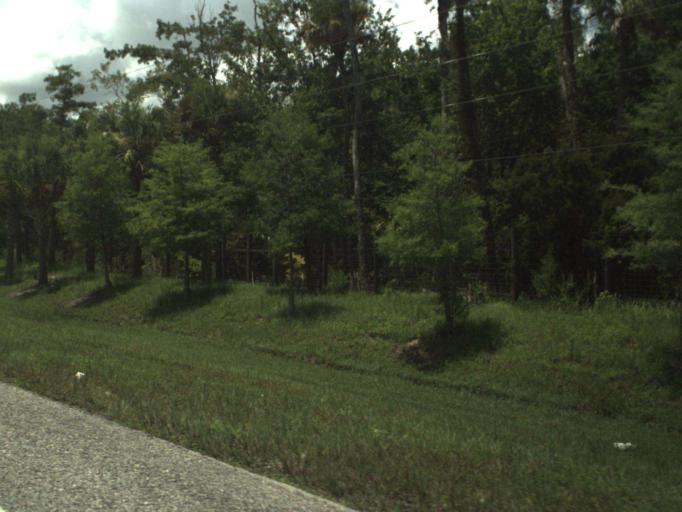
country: US
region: Florida
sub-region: Indian River County
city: Fellsmere
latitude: 27.6676
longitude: -80.8011
